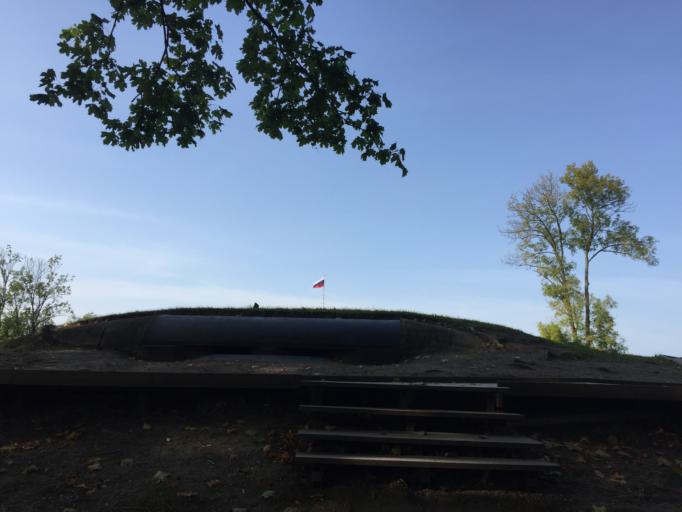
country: RU
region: Kaliningrad
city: Bol'shoe Isakovo
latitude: 54.6563
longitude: 20.5680
